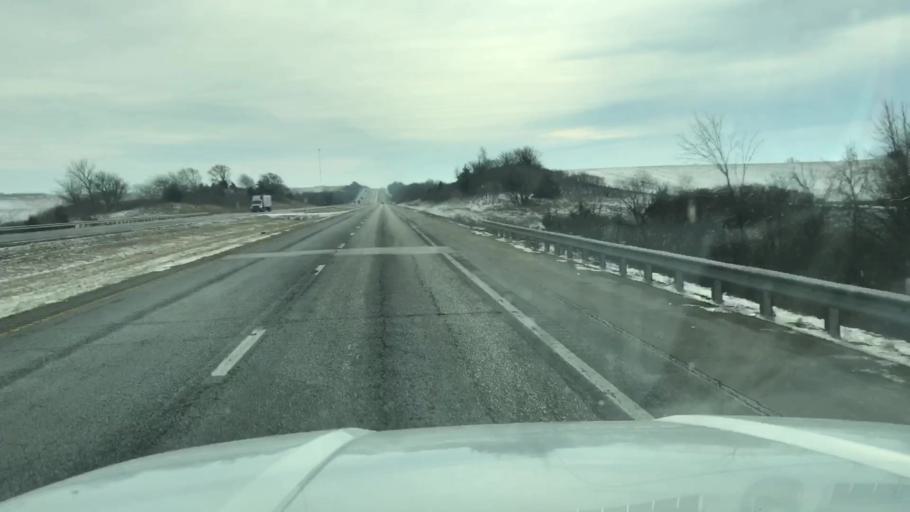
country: US
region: Missouri
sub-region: Holt County
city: Oregon
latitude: 40.0129
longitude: -95.0825
